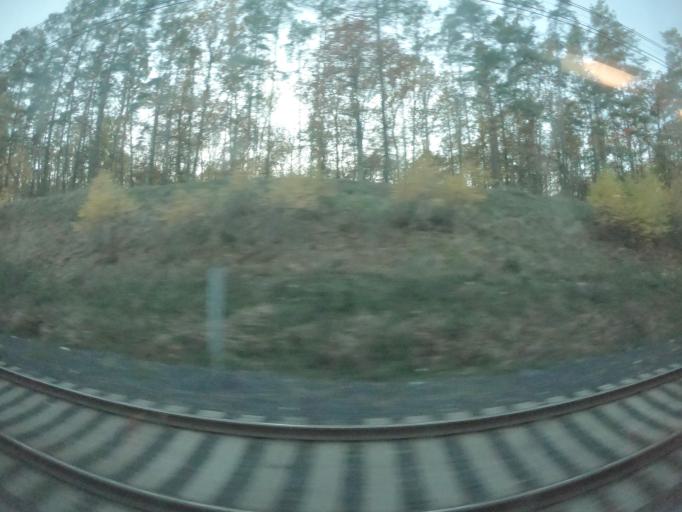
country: PL
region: West Pomeranian Voivodeship
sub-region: Powiat mysliborski
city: Boleszkowice
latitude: 52.7198
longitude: 14.5293
